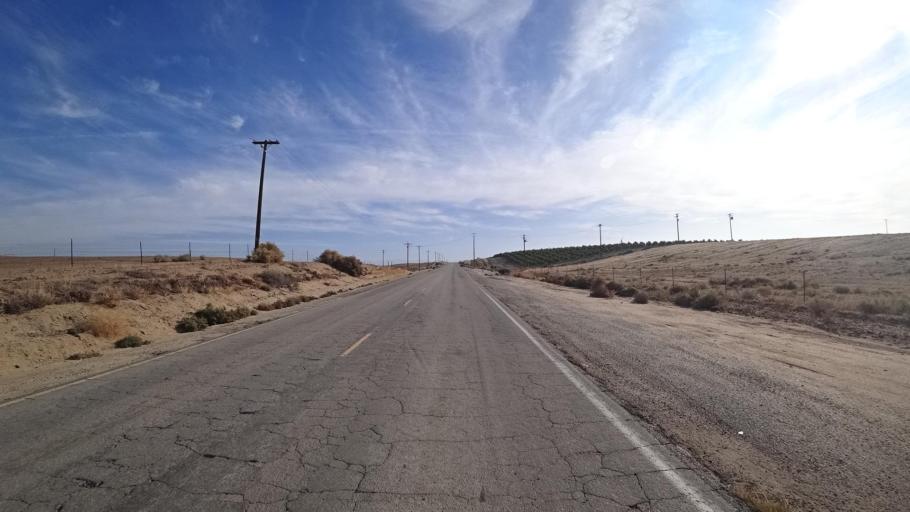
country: US
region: California
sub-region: Kern County
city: McFarland
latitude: 35.6025
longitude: -119.0823
